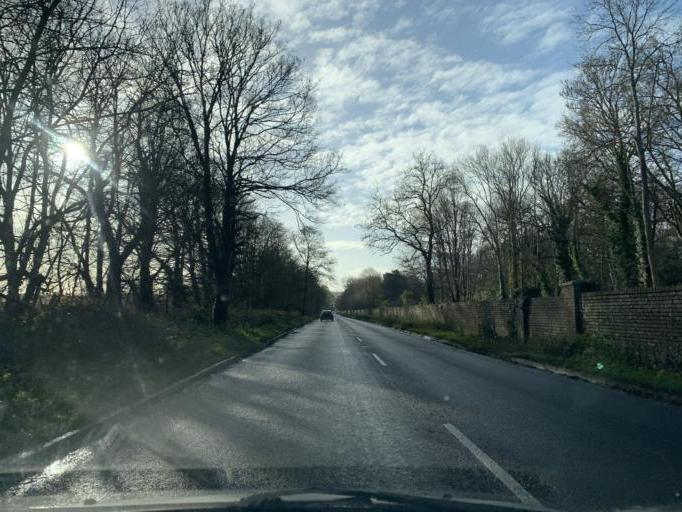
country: GB
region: England
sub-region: Wiltshire
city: Wilton
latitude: 51.0744
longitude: -1.8505
